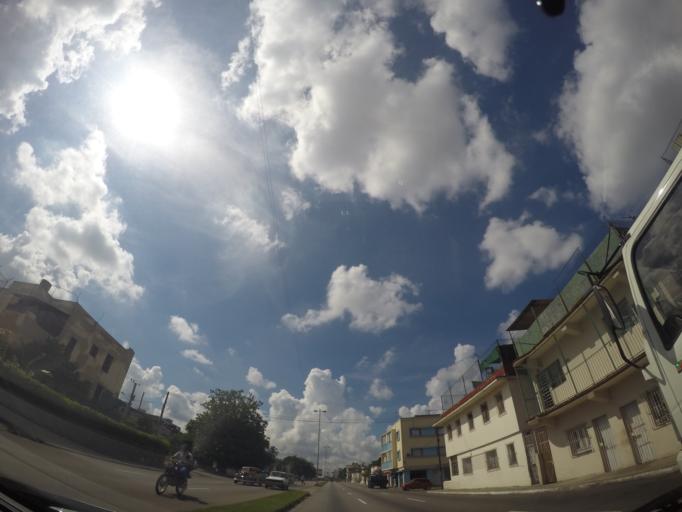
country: CU
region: La Habana
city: Cerro
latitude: 23.0975
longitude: -82.4213
